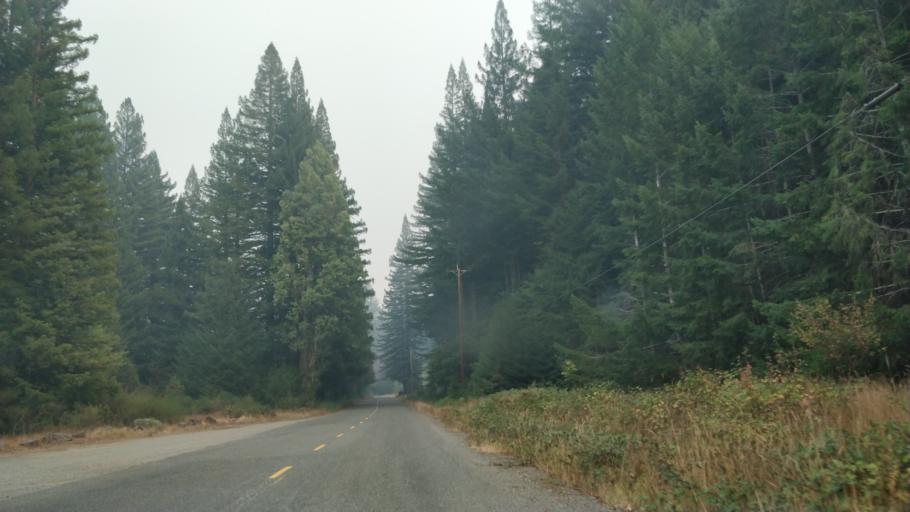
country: US
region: California
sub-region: Humboldt County
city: Rio Dell
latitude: 40.3505
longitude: -124.0155
